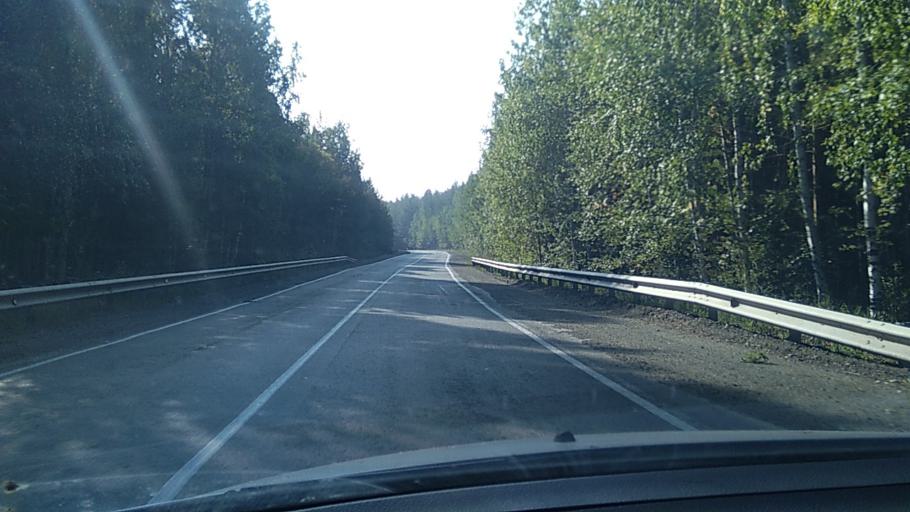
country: RU
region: Chelyabinsk
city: Karabash
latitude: 55.4287
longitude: 60.2573
